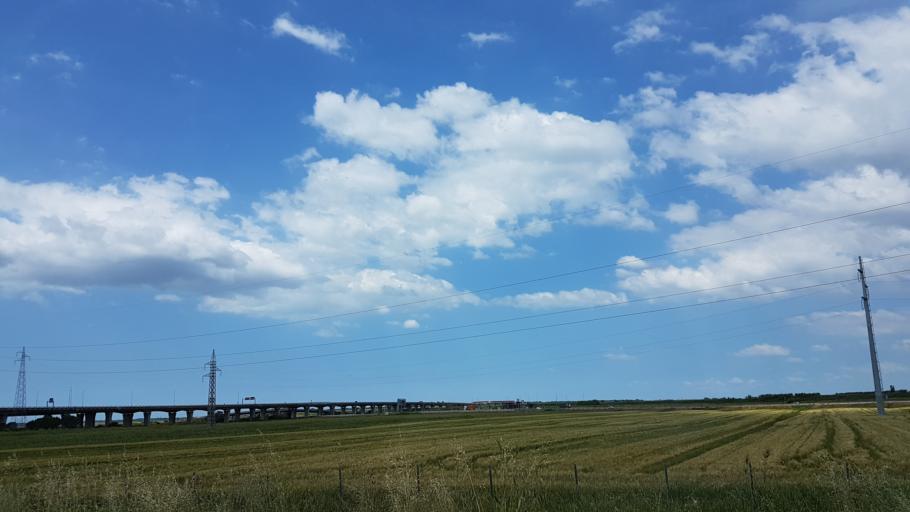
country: IT
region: Tuscany
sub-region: Provincia di Livorno
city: Vicarello
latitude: 43.6148
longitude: 10.4445
